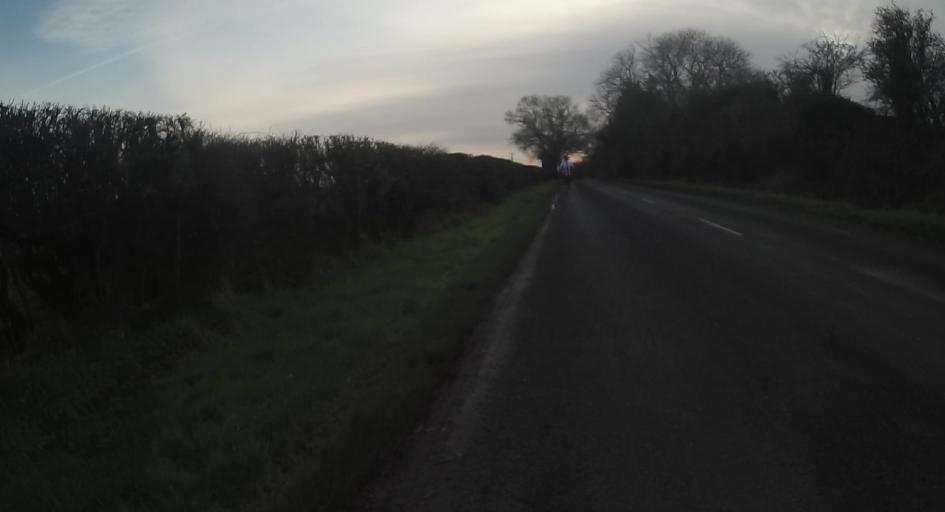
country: GB
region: England
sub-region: Hampshire
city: Overton
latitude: 51.2531
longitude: -1.3308
